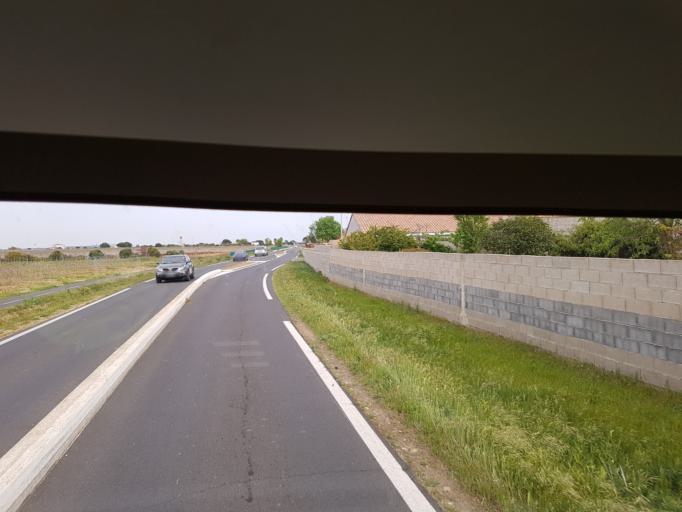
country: FR
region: Languedoc-Roussillon
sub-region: Departement de l'Herault
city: Vendres
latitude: 43.2705
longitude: 3.2407
